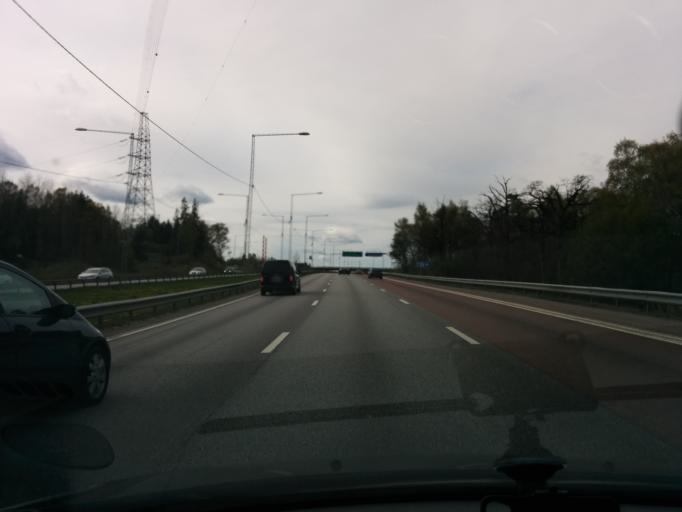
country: SE
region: Stockholm
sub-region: Huddinge Kommun
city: Segeltorp
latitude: 59.2663
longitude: 17.9021
